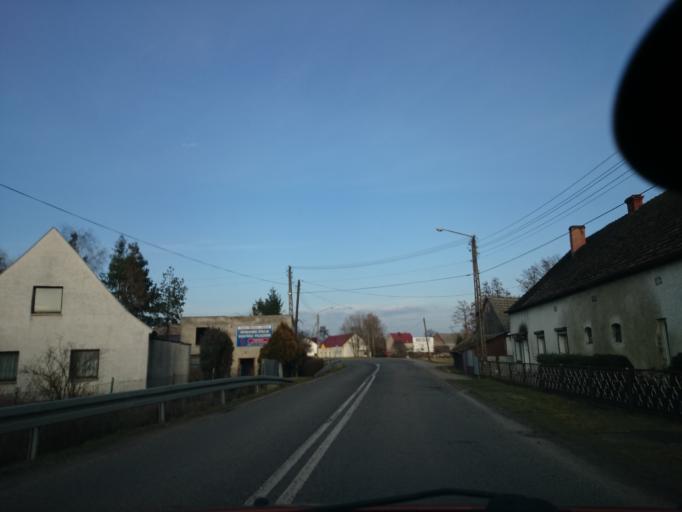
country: PL
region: Opole Voivodeship
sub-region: Powiat opolski
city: Popielow
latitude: 50.8144
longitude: 17.7353
